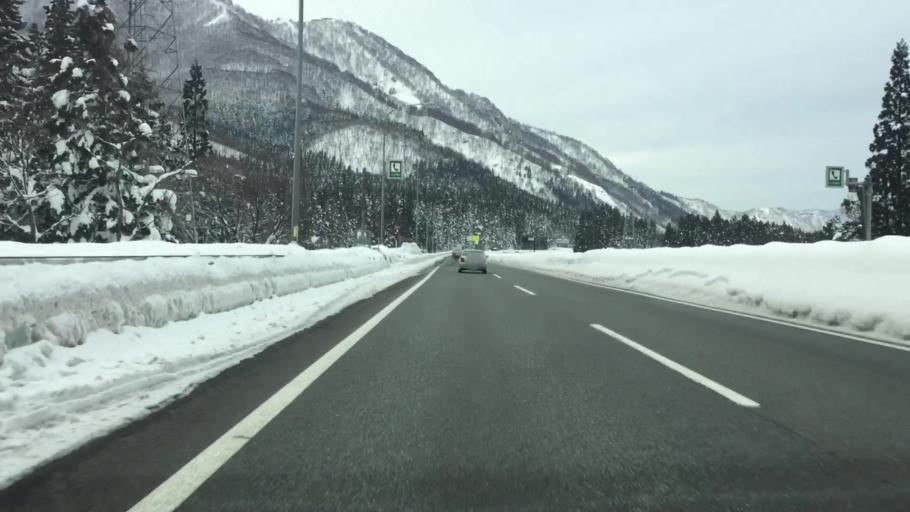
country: JP
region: Niigata
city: Shiozawa
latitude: 36.8792
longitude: 138.8568
